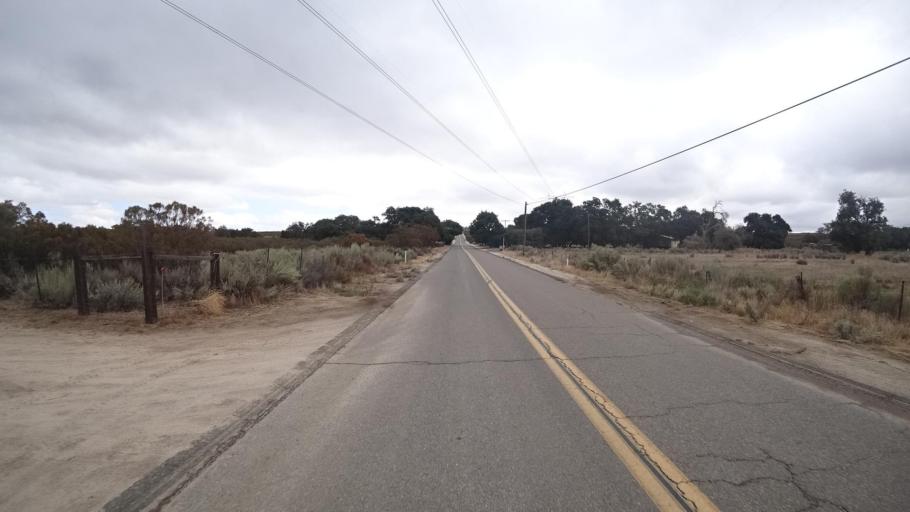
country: US
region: California
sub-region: San Diego County
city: Campo
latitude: 32.6046
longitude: -116.3480
